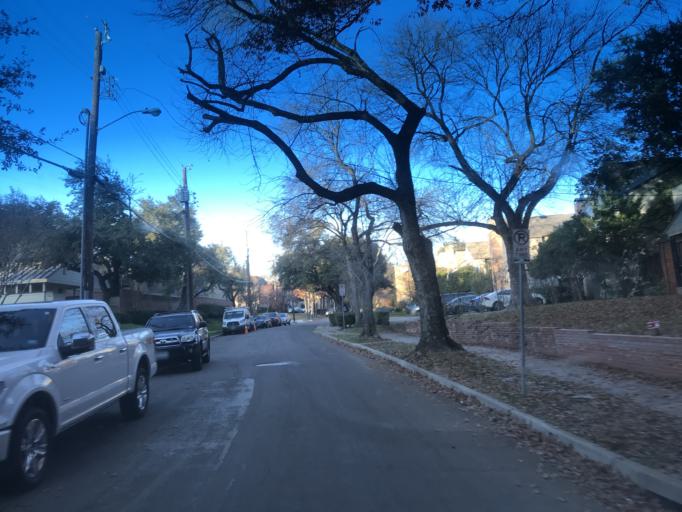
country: US
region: Texas
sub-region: Dallas County
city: Highland Park
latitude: 32.8122
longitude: -96.7974
